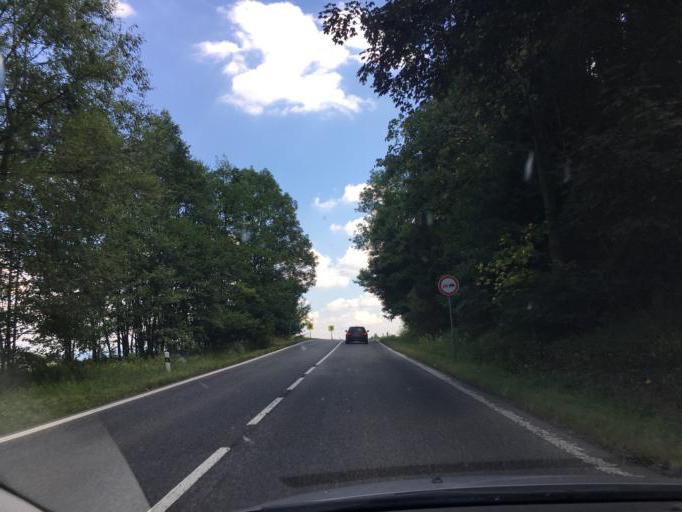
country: CZ
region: Ustecky
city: Benesov nad Ploucnici
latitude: 50.7898
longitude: 14.3221
